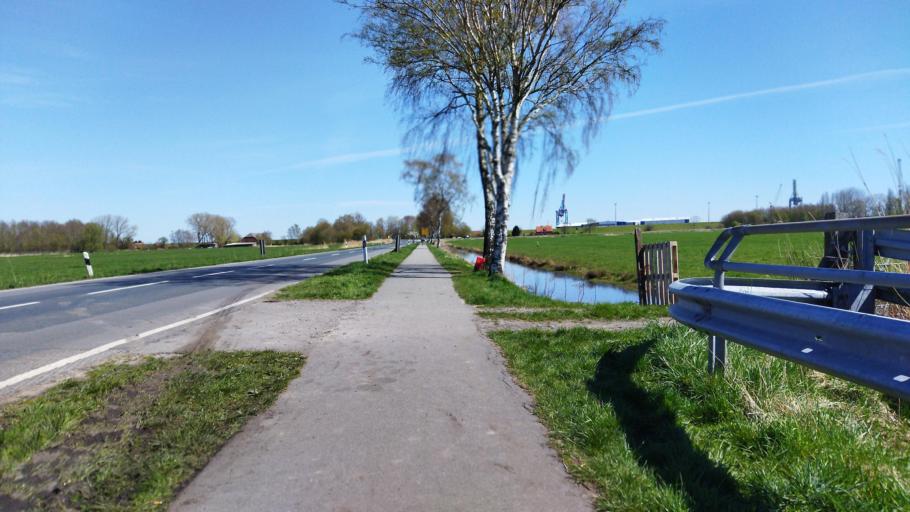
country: DE
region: Lower Saxony
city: Brake (Unterweser)
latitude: 53.3547
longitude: 8.4773
